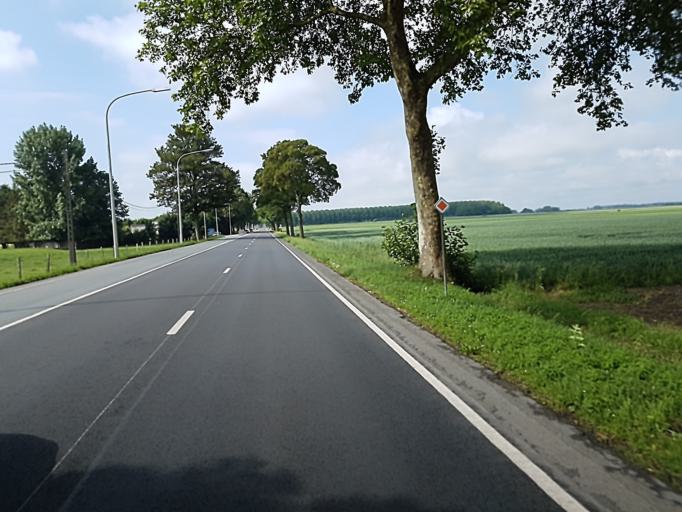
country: BE
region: Wallonia
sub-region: Province du Hainaut
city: Soignies
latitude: 50.5268
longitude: 4.0267
